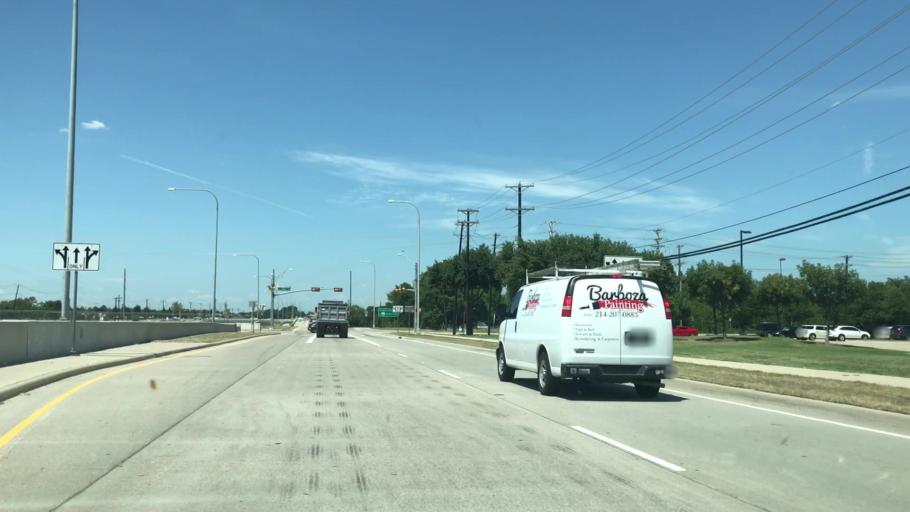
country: US
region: Texas
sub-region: Dallas County
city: Rowlett
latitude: 32.9024
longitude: -96.5555
